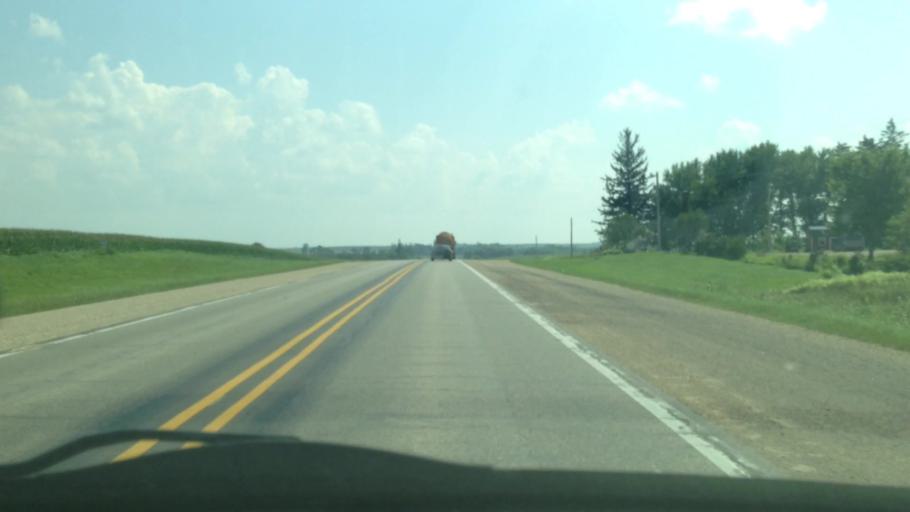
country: US
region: Iowa
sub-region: Chickasaw County
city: New Hampton
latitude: 43.2198
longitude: -92.2984
